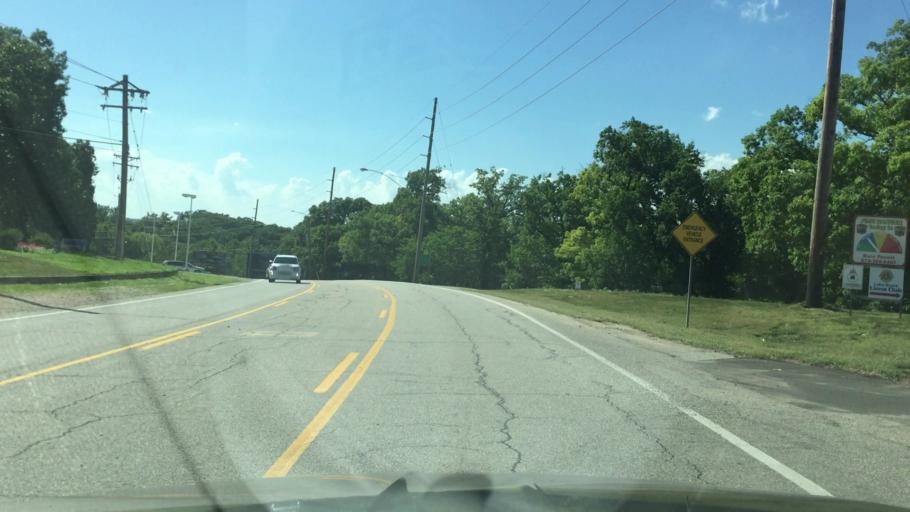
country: US
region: Missouri
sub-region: Miller County
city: Lake Ozark
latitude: 38.1796
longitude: -92.6215
